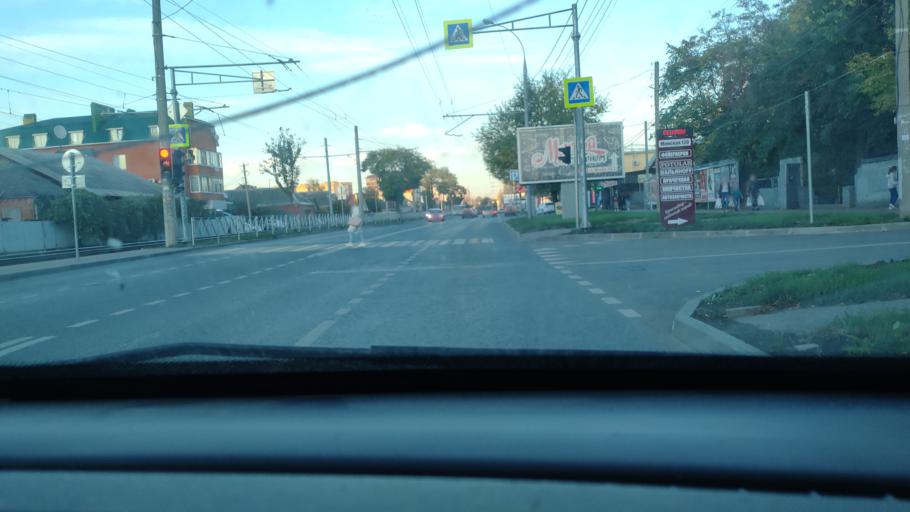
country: RU
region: Krasnodarskiy
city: Krasnodar
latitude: 45.0373
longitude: 38.9298
